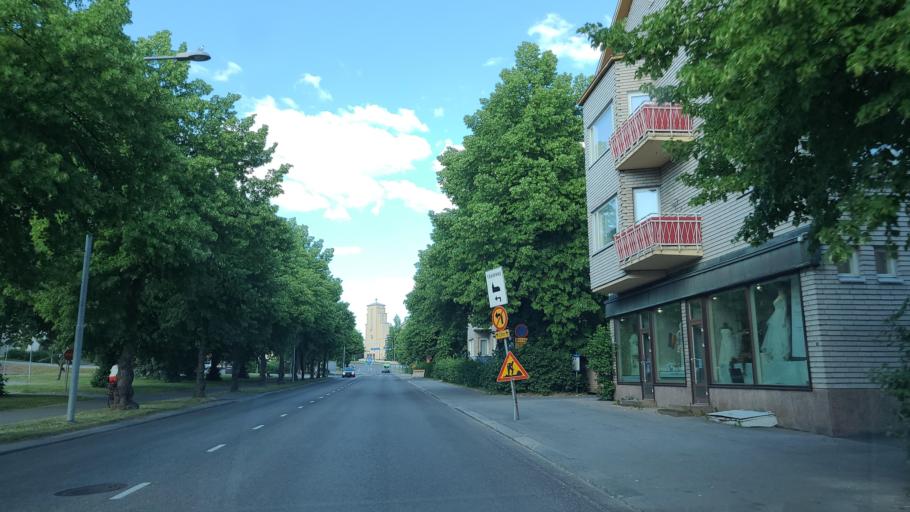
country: FI
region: Central Finland
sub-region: Jyvaeskylae
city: Jyvaeskylae
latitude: 62.2510
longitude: 25.7452
